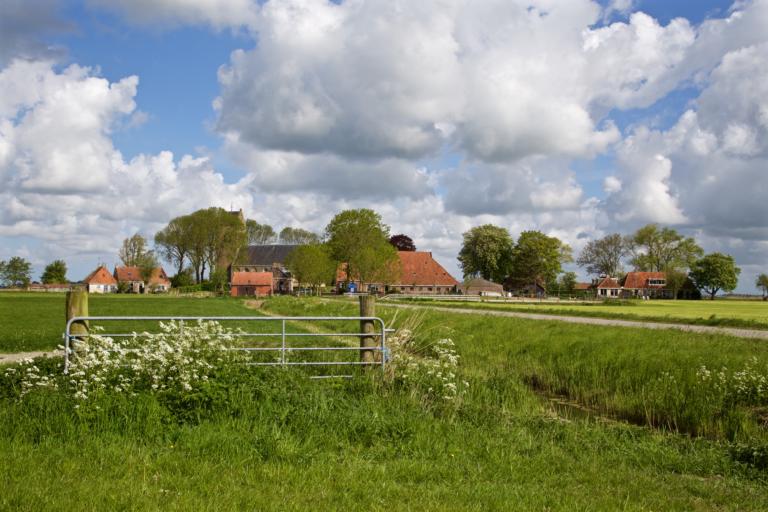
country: NL
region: Friesland
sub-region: Gemeente Littenseradiel
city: Makkum
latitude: 53.0870
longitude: 5.6648
